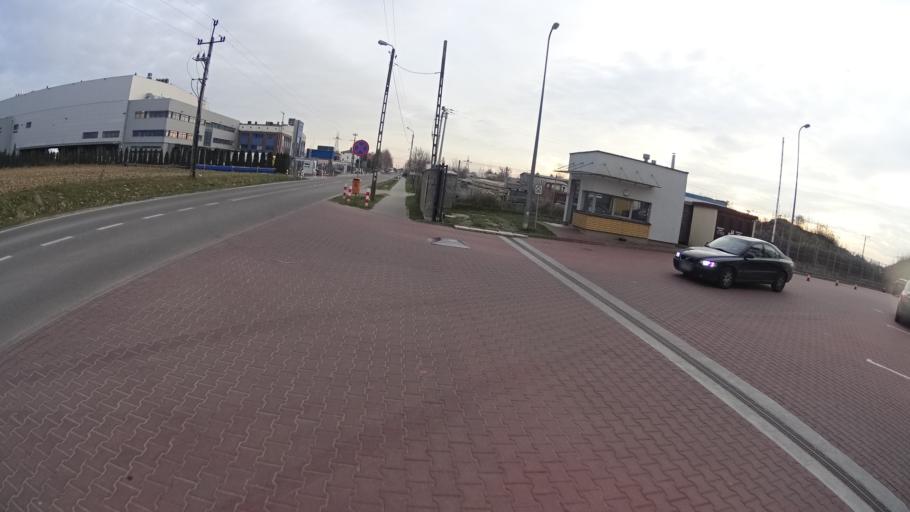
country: PL
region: Masovian Voivodeship
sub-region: Powiat warszawski zachodni
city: Babice
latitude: 52.2188
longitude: 20.8598
